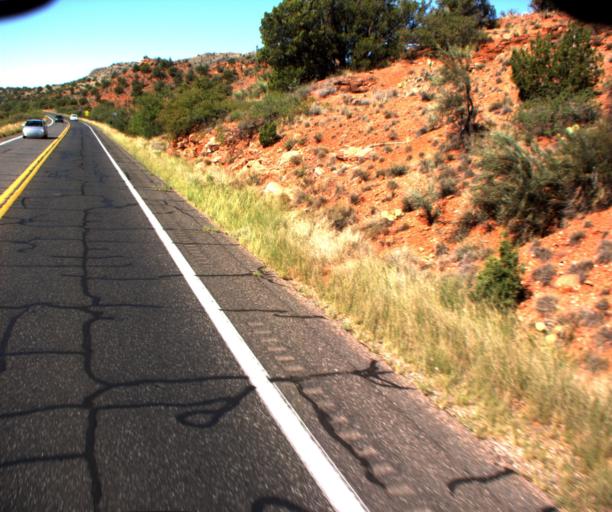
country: US
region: Arizona
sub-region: Yavapai County
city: Big Park
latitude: 34.7406
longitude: -111.7716
